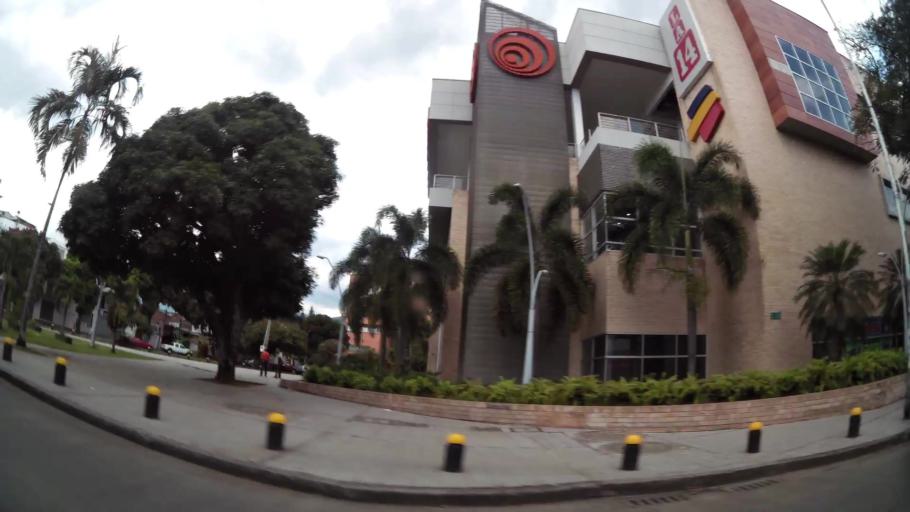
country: CO
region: Valle del Cauca
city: Cali
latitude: 3.4267
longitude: -76.5373
